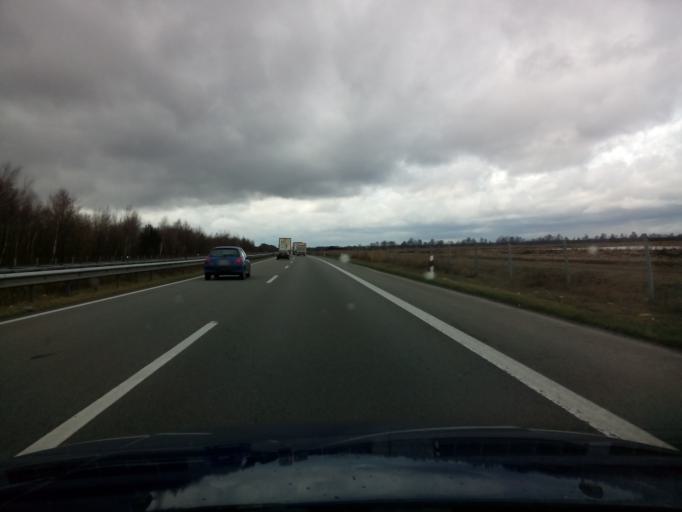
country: DE
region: Lower Saxony
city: Haren
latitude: 52.7227
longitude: 7.1384
